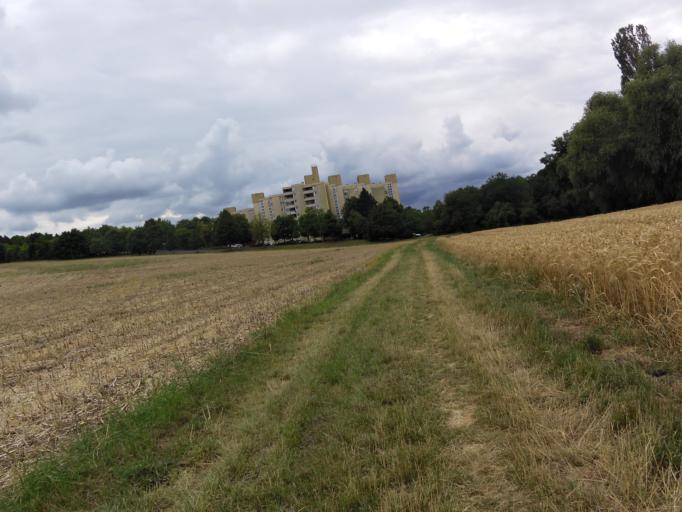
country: DE
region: Bavaria
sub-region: Regierungsbezirk Unterfranken
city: Estenfeld
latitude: 49.8151
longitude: 9.9764
